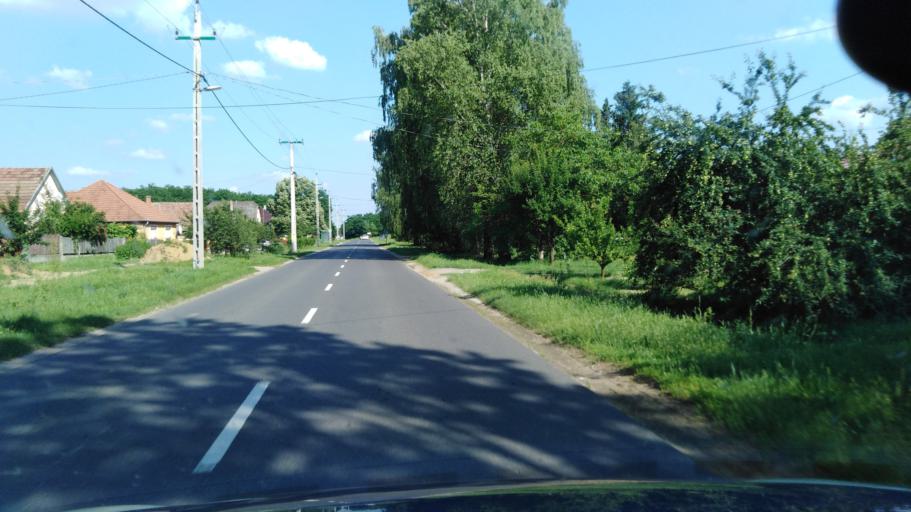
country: HU
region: Szabolcs-Szatmar-Bereg
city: Nyirvasvari
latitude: 47.8132
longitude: 22.2003
